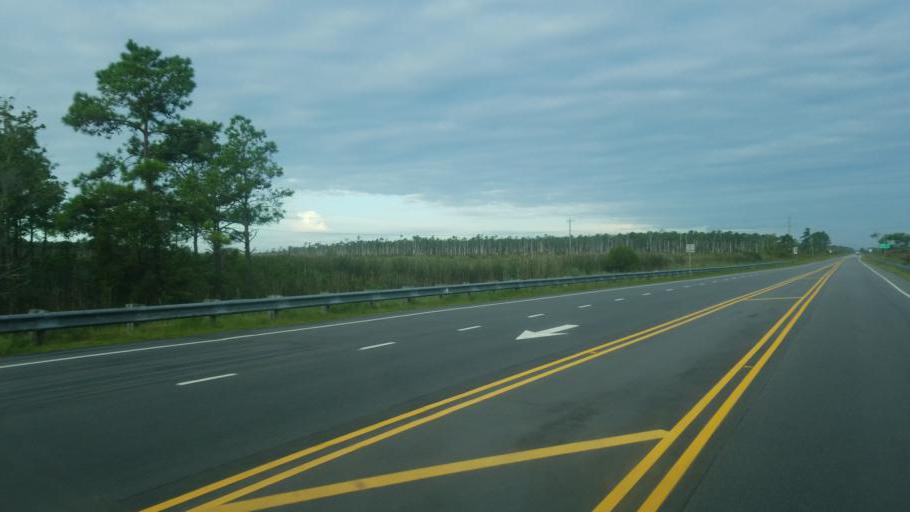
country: US
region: North Carolina
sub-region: Dare County
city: Manteo
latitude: 35.8713
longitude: -75.7858
